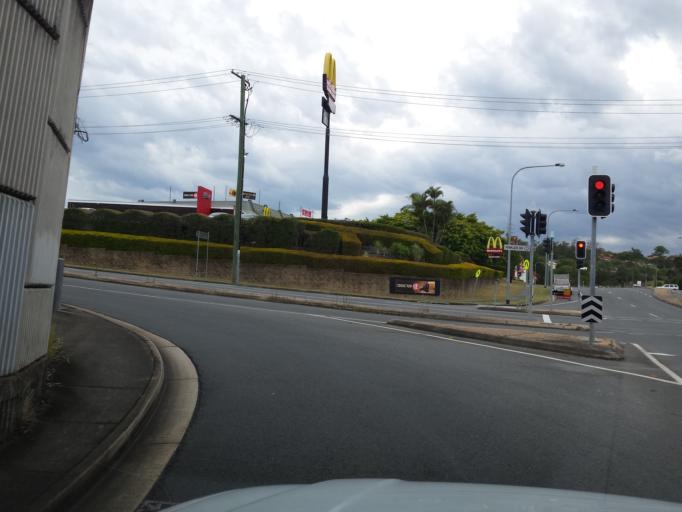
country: AU
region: Queensland
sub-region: Gold Coast
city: Nerang
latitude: -28.0073
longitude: 153.3425
